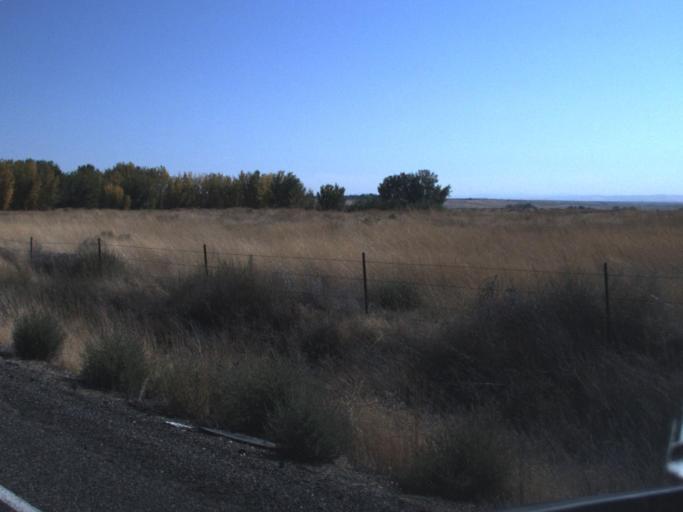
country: US
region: Washington
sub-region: Walla Walla County
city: Burbank
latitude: 46.2118
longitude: -118.9685
